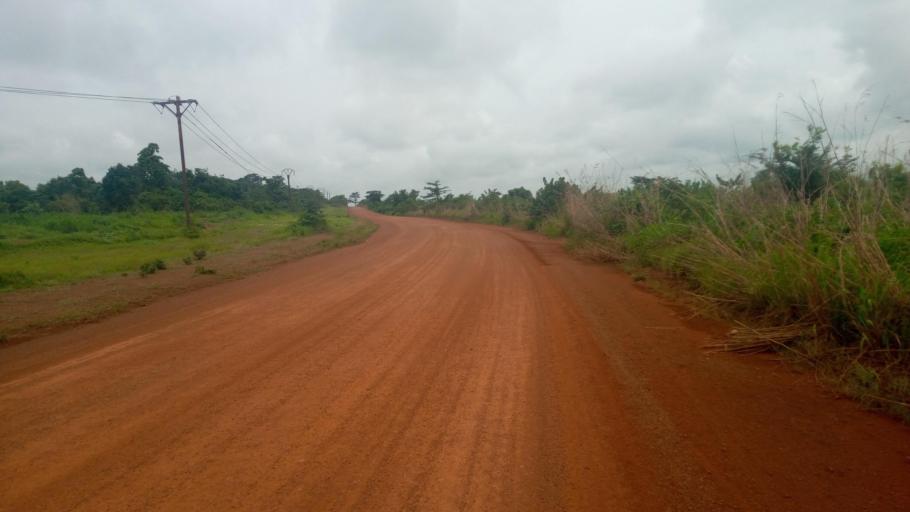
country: SL
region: Southern Province
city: Mogbwemo
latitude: 7.7376
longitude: -12.2805
